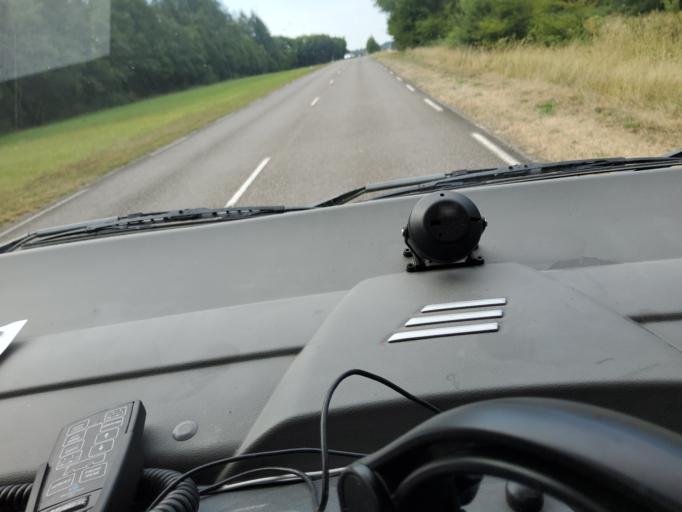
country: FR
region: Franche-Comte
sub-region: Departement du Jura
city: Mont-sous-Vaudrey
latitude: 46.9714
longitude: 5.5103
